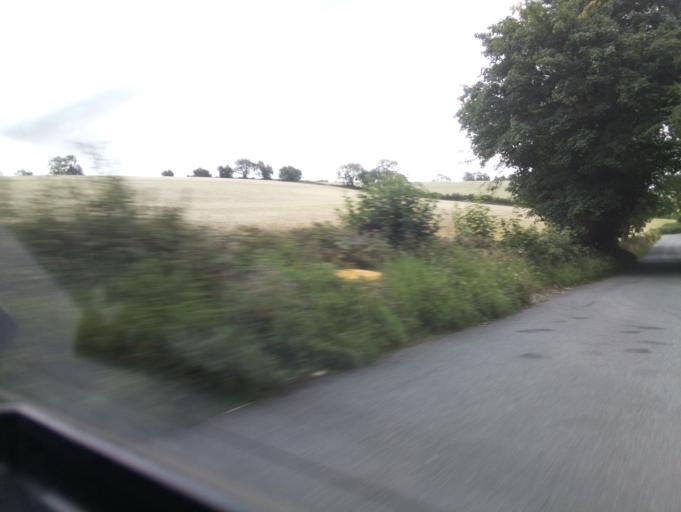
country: GB
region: England
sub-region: Gloucestershire
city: Shurdington
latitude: 51.7910
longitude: -2.1177
